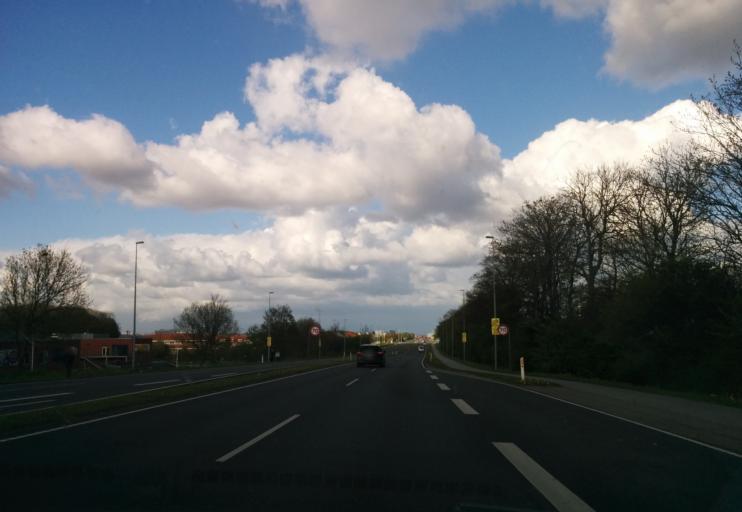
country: DK
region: Central Jutland
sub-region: Arhus Kommune
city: Stavtrup
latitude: 56.1122
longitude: 10.1264
